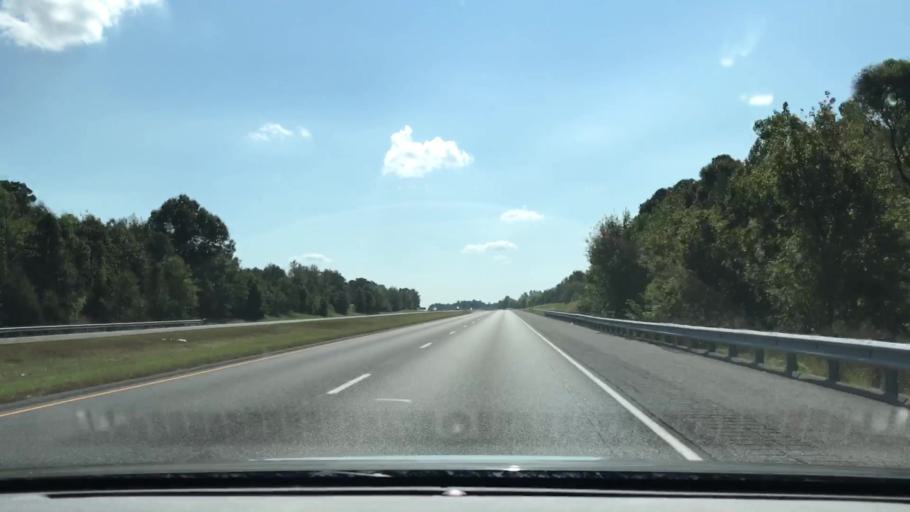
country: US
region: Kentucky
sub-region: Marshall County
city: Benton
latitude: 36.8025
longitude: -88.3421
